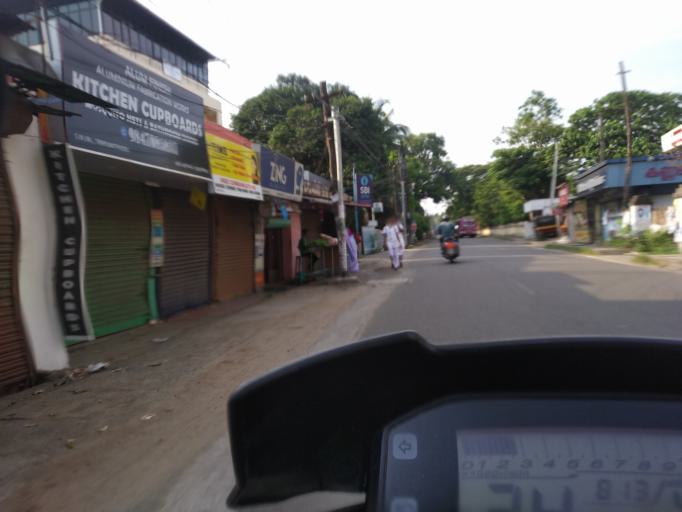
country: IN
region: Kerala
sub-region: Ernakulam
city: Cochin
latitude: 9.9530
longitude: 76.3454
